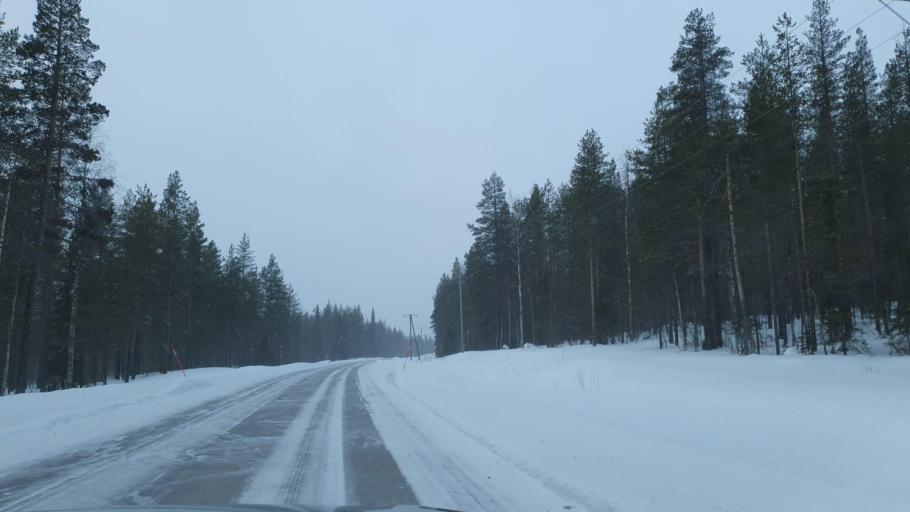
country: FI
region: Lapland
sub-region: Tunturi-Lappi
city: Kolari
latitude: 67.4448
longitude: 23.8419
